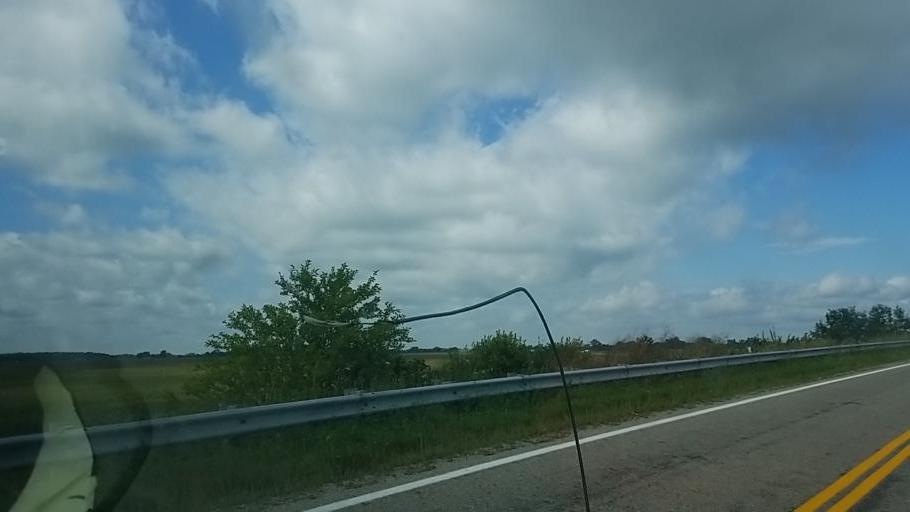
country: US
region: Ohio
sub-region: Madison County
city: Bethel
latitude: 39.7292
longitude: -83.3712
